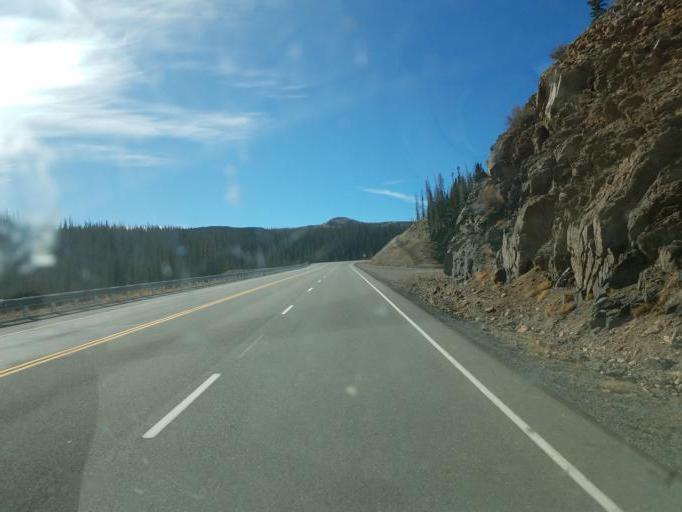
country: US
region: Colorado
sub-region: Archuleta County
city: Pagosa Springs
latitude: 37.4817
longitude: -106.7705
